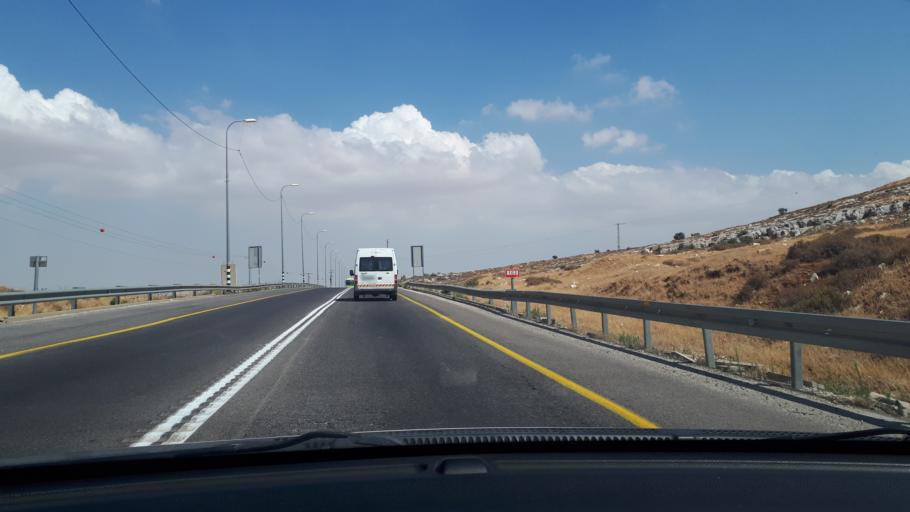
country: PS
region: West Bank
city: Burqah
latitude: 31.8940
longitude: 35.2718
